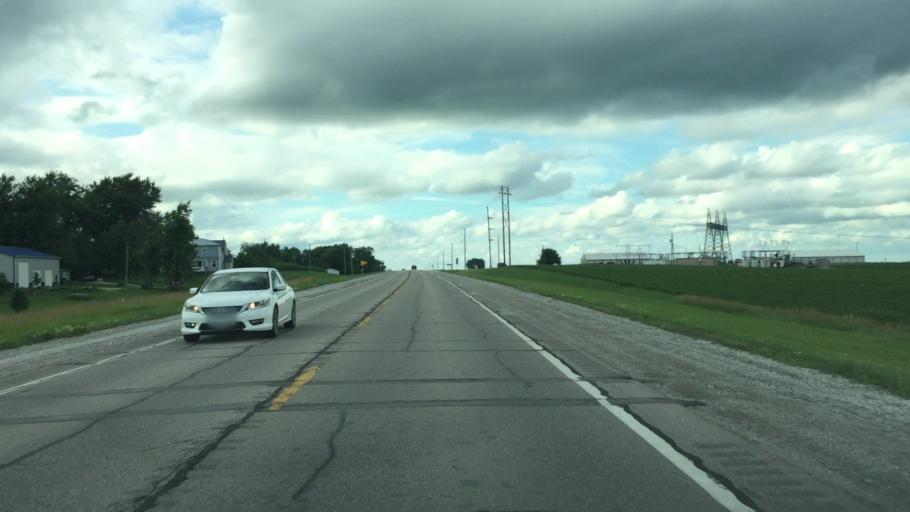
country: US
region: Iowa
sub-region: Jasper County
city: Monroe
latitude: 41.5700
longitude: -93.0969
